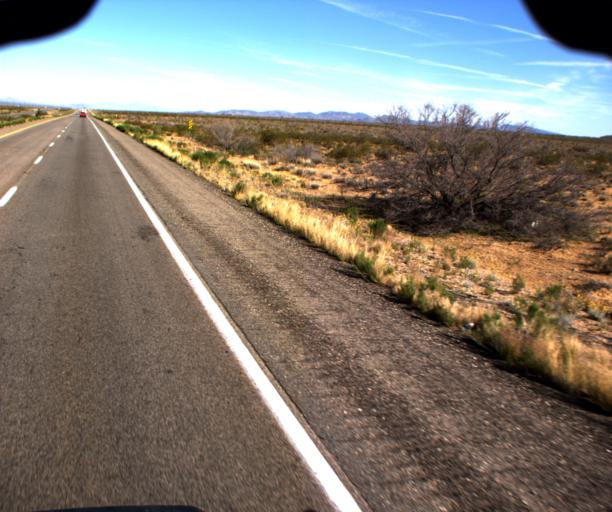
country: US
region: Arizona
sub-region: Mohave County
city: Dolan Springs
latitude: 35.4698
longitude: -114.3108
